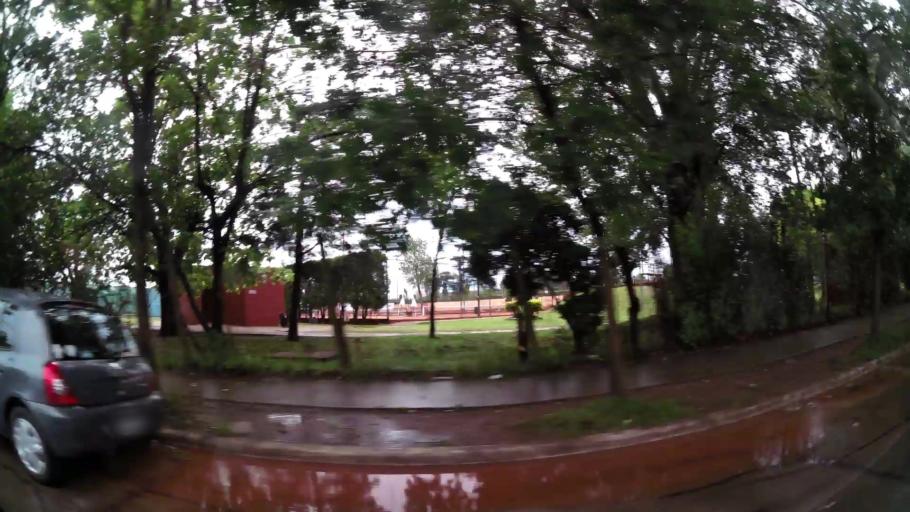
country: AR
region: Buenos Aires F.D.
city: Villa Lugano
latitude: -34.6527
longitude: -58.4465
